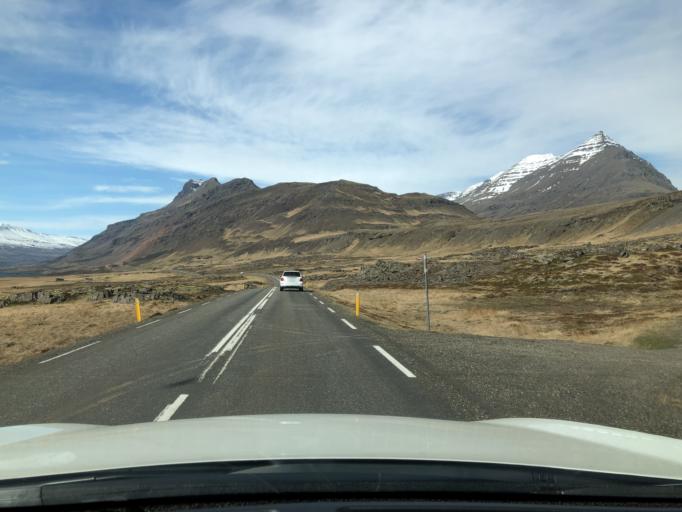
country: IS
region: East
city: Reydarfjoerdur
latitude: 64.6563
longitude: -14.3552
